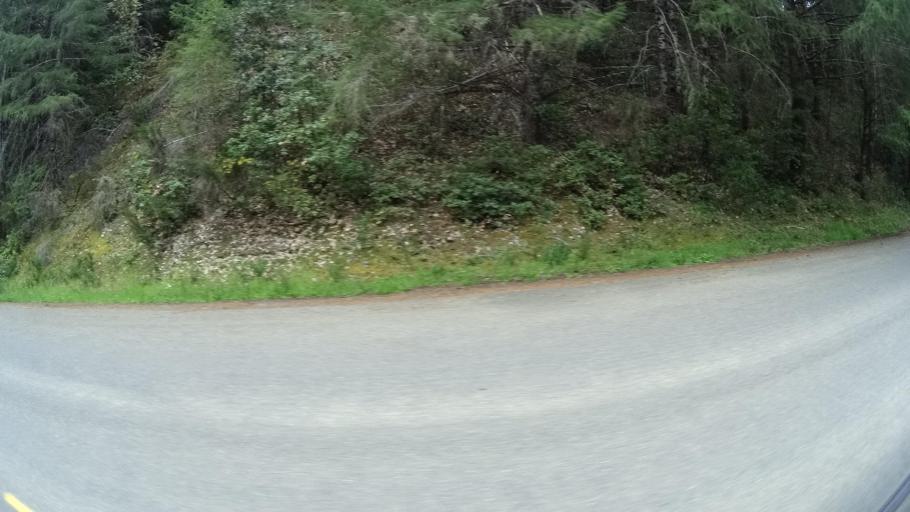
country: US
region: California
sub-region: Humboldt County
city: Redway
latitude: 40.1053
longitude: -123.9221
